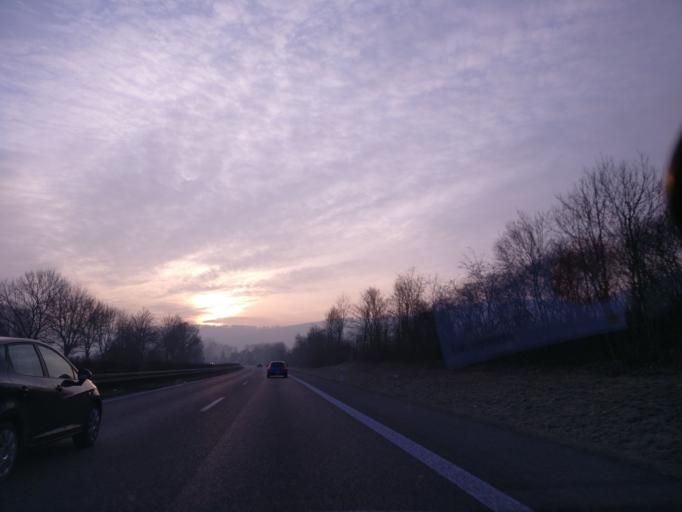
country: DE
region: Baden-Wuerttemberg
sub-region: Regierungsbezirk Stuttgart
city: Pluderhausen
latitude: 48.7850
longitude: 9.6055
